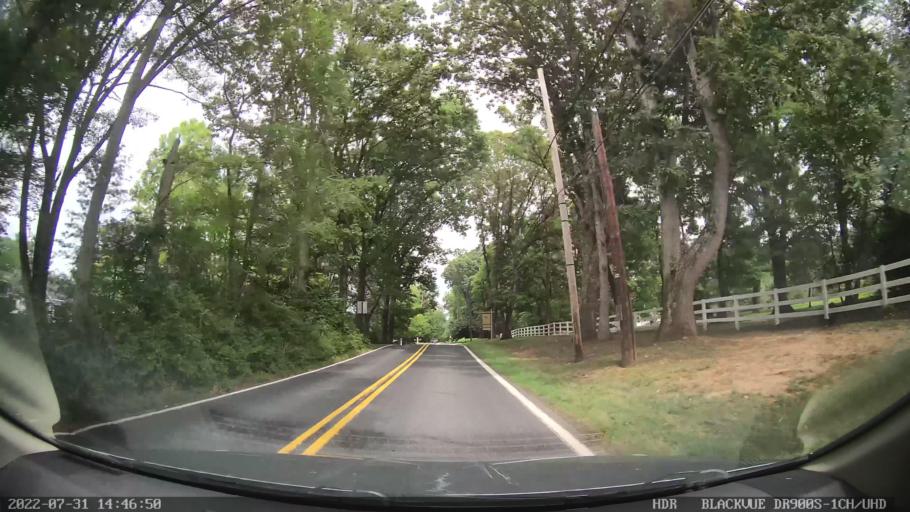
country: US
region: Pennsylvania
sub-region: Northampton County
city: Hellertown
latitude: 40.5679
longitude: -75.3728
